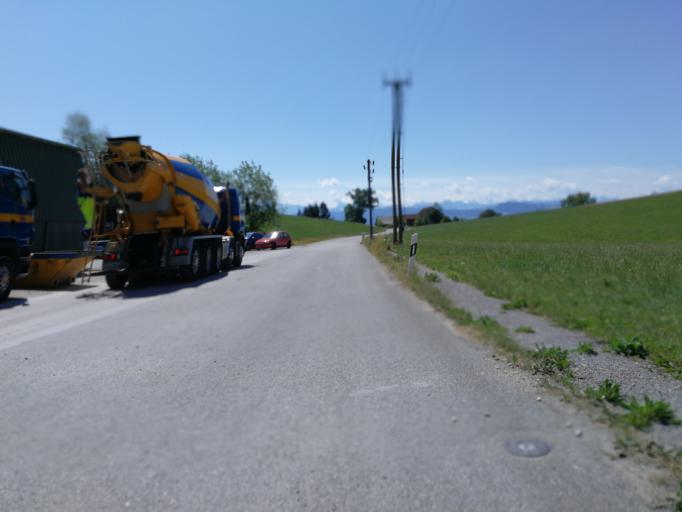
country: CH
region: Zurich
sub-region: Bezirk Hinwil
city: Gossau
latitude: 47.3138
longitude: 8.7521
